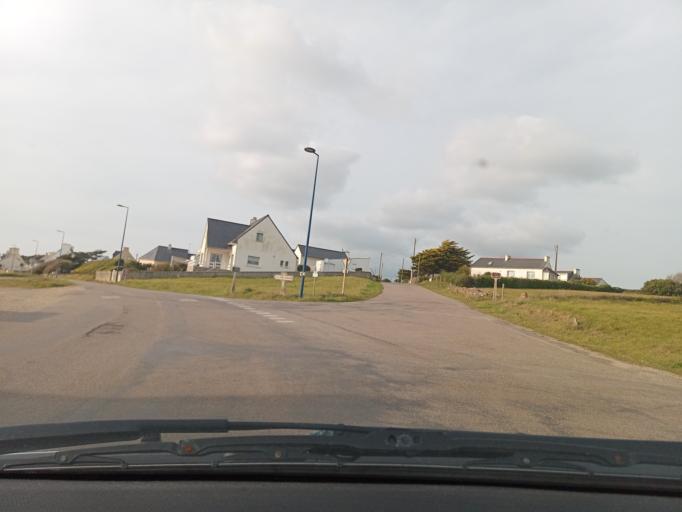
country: FR
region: Brittany
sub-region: Departement du Finistere
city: Plozevet
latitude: 47.9811
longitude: -4.4498
